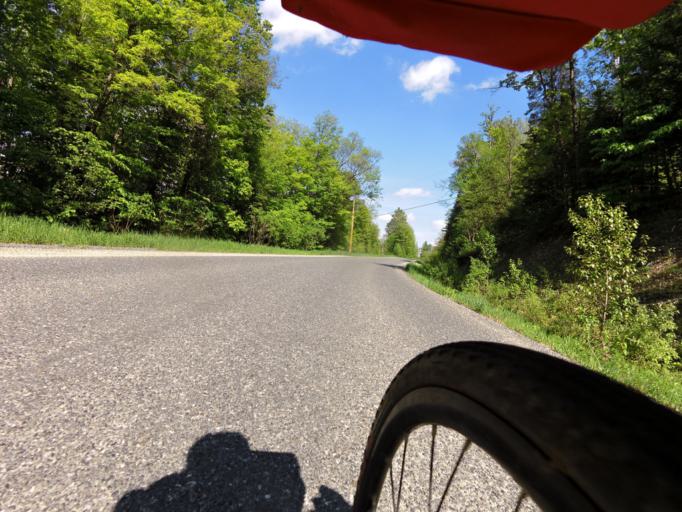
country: CA
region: Ontario
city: Renfrew
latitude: 45.1458
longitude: -76.5678
